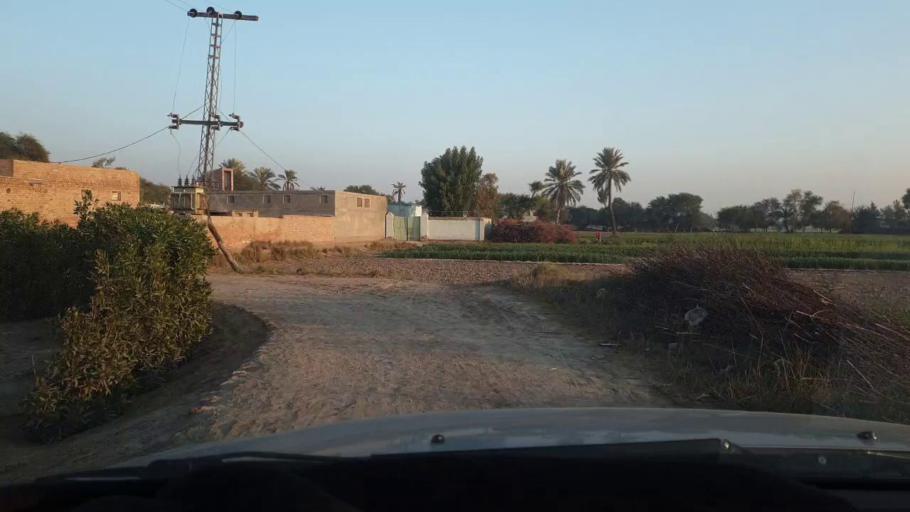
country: PK
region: Sindh
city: Mirpur Mathelo
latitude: 27.9944
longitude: 69.6036
